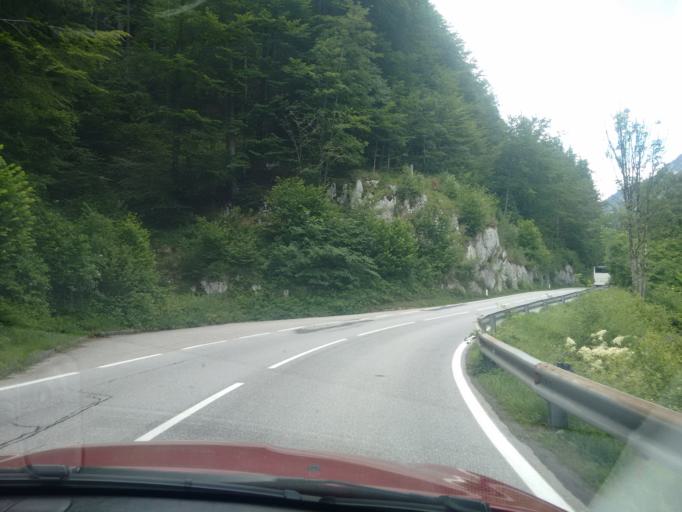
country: AT
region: Upper Austria
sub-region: Politischer Bezirk Gmunden
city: Bad Goisern
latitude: 47.5785
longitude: 13.6556
